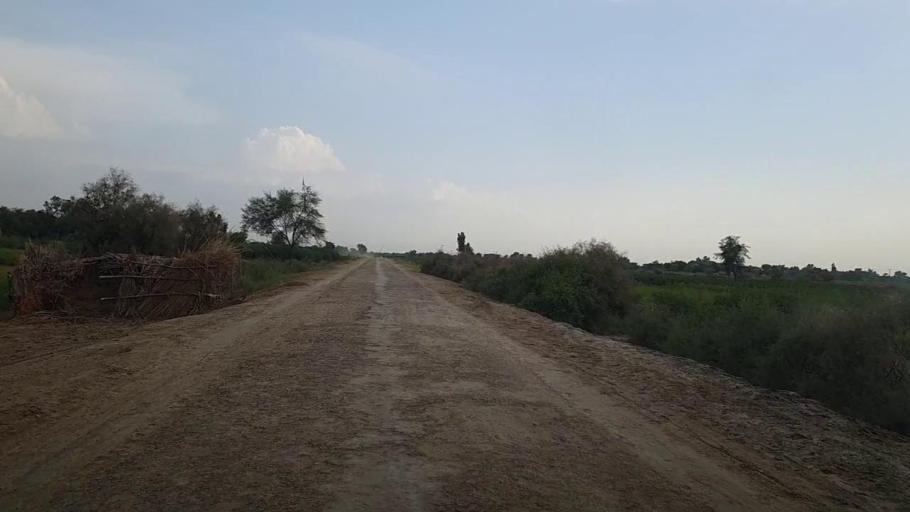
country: PK
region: Sindh
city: Khanpur
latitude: 27.8663
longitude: 69.4881
